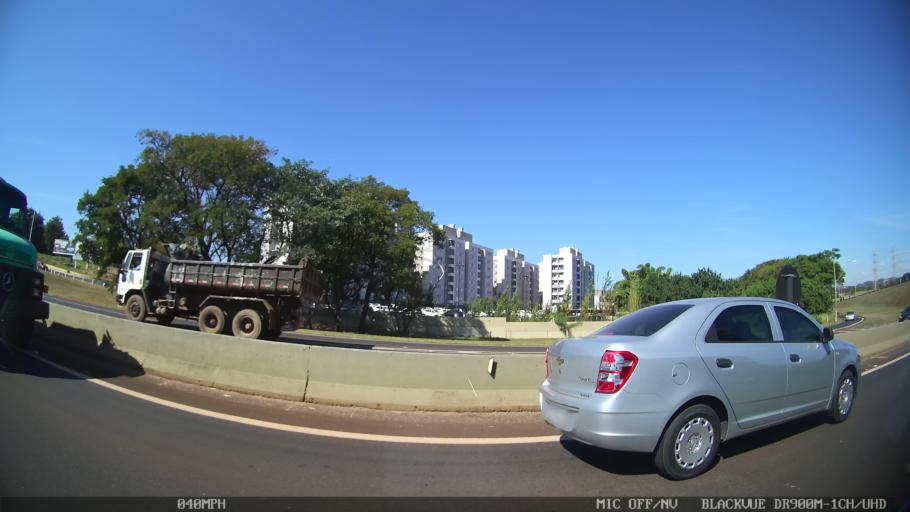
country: BR
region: Sao Paulo
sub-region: Ribeirao Preto
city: Ribeirao Preto
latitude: -21.2142
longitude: -47.7727
